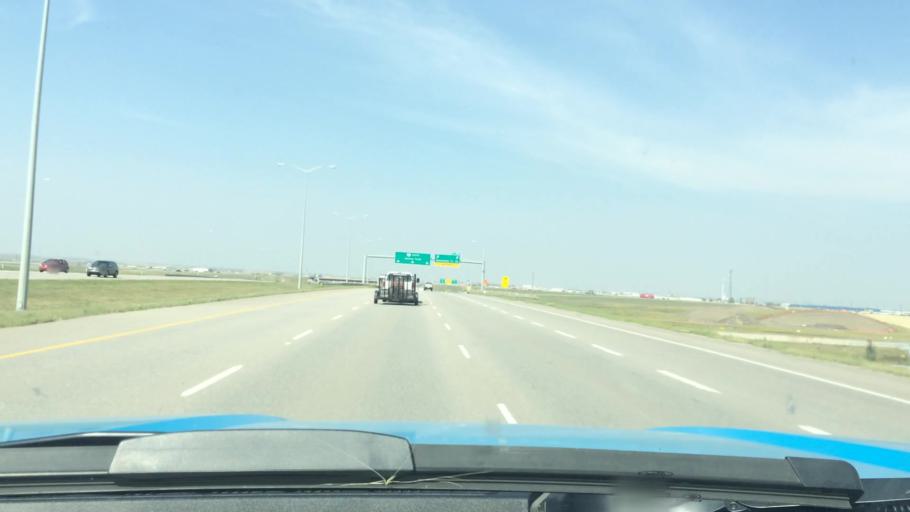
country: CA
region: Alberta
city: Chestermere
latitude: 50.9707
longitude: -113.9203
